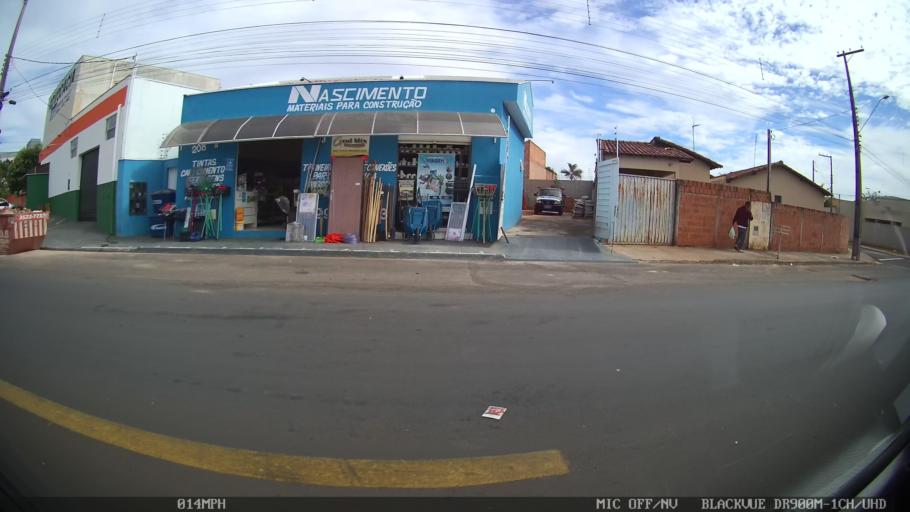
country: BR
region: Sao Paulo
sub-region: Catanduva
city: Catanduva
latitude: -21.1608
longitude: -48.9702
